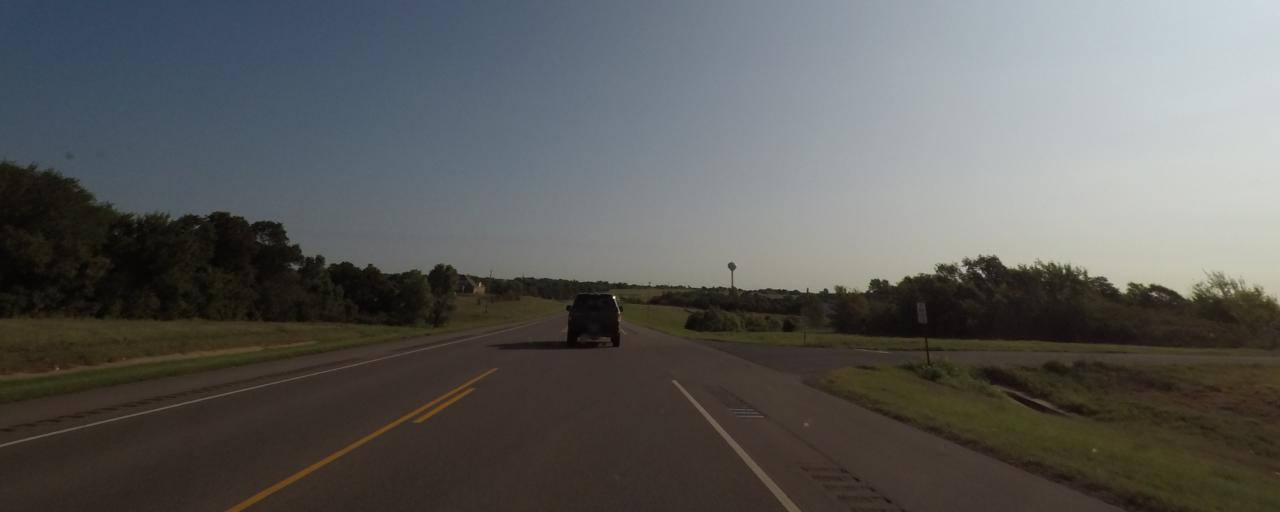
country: US
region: Oklahoma
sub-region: McClain County
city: Blanchard
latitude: 35.1168
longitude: -97.7084
